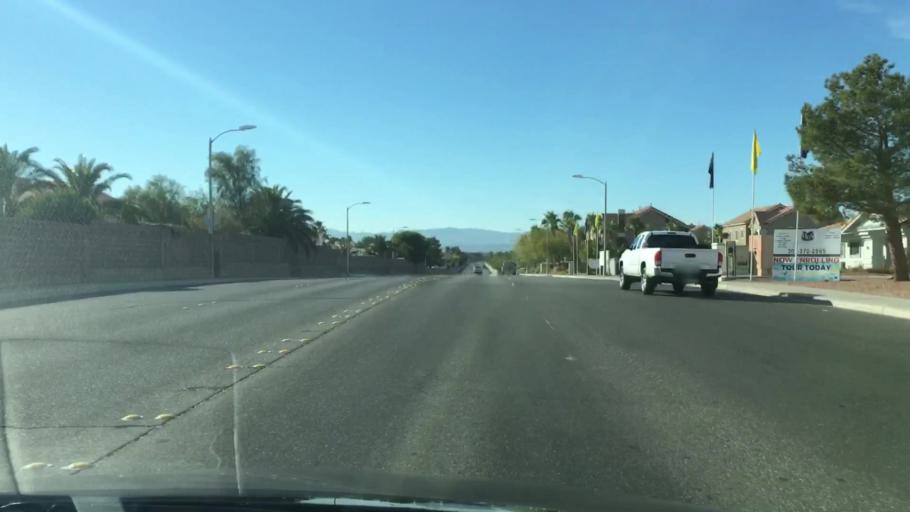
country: US
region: Nevada
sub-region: Clark County
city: Whitney
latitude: 36.0497
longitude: -115.1063
